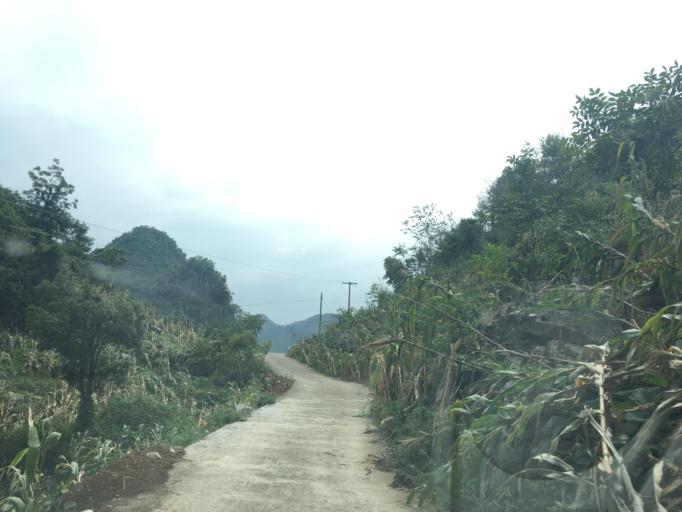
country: CN
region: Guangxi Zhuangzu Zizhiqu
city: Xinzhou
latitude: 25.2281
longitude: 105.6402
